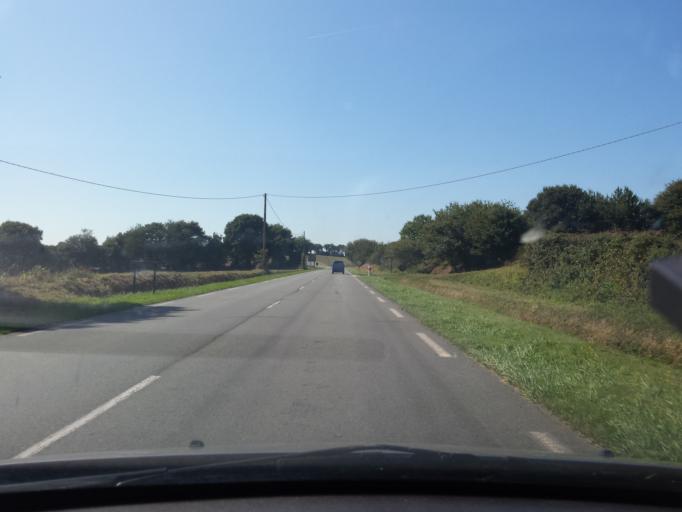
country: FR
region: Brittany
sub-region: Departement des Cotes-d'Armor
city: Corlay
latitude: 48.3161
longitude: -3.1095
